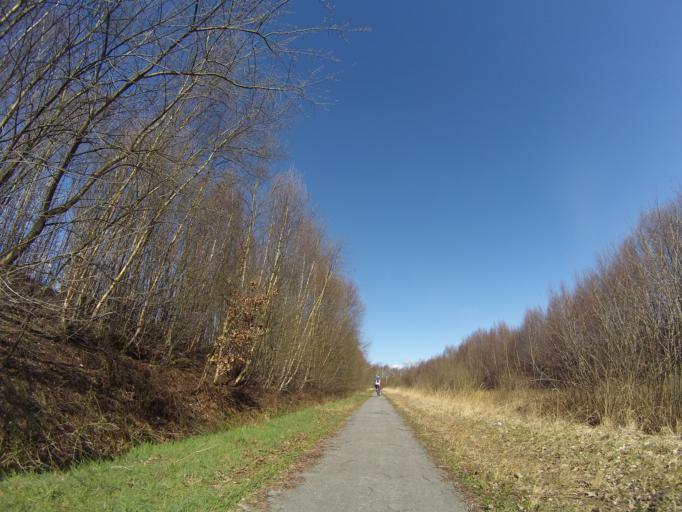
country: NL
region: Drenthe
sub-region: Gemeente Emmen
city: Klazienaveen
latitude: 52.7594
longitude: 6.9854
